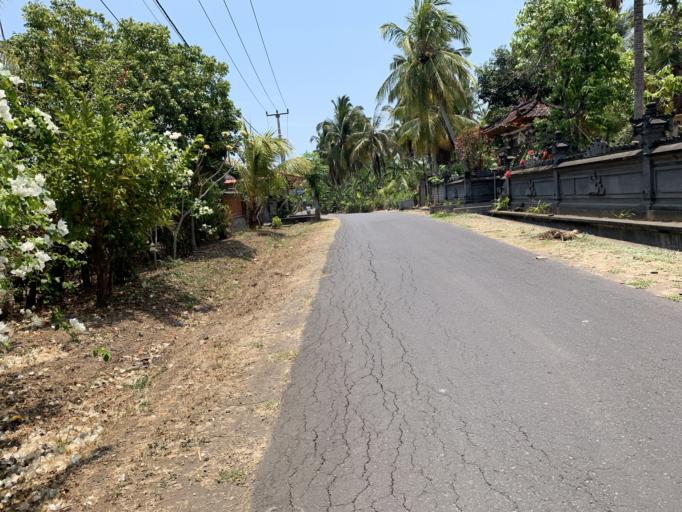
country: ID
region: Bali
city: Banjar Dangin Pangkung
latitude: -8.4314
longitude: 114.8279
